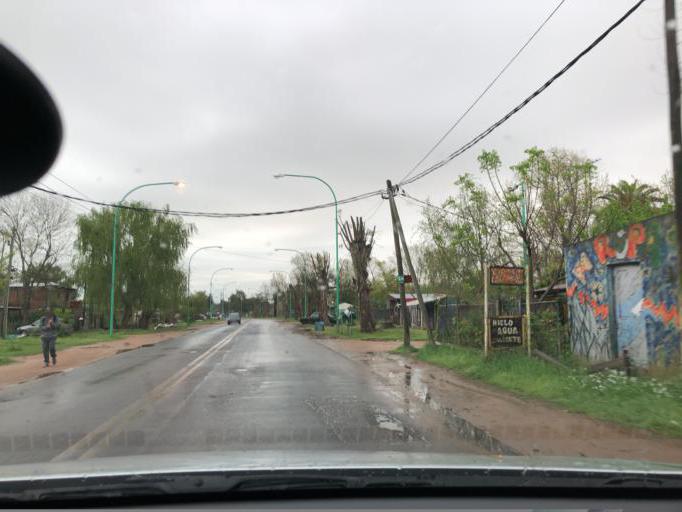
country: AR
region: Buenos Aires
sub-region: Partido de Ensenada
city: Ensenada
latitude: -34.8374
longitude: -57.9422
